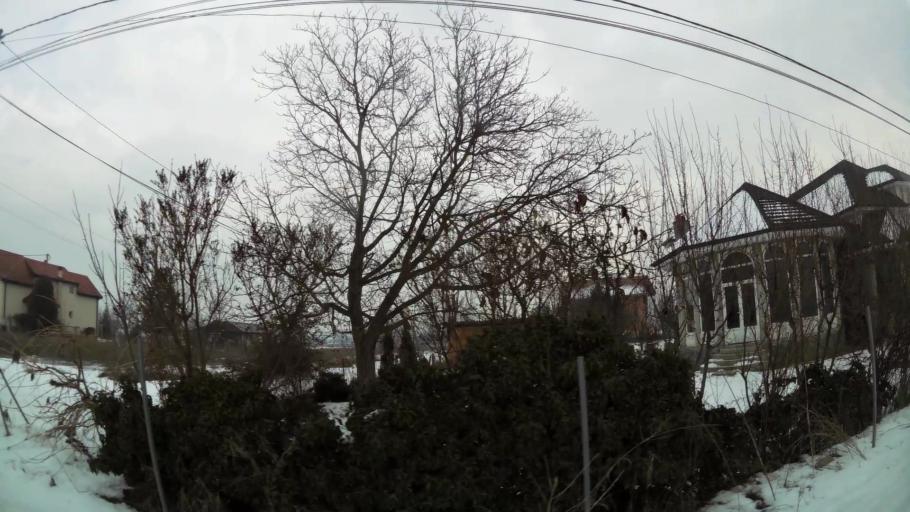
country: MK
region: Saraj
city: Saraj
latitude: 42.0402
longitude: 21.3584
